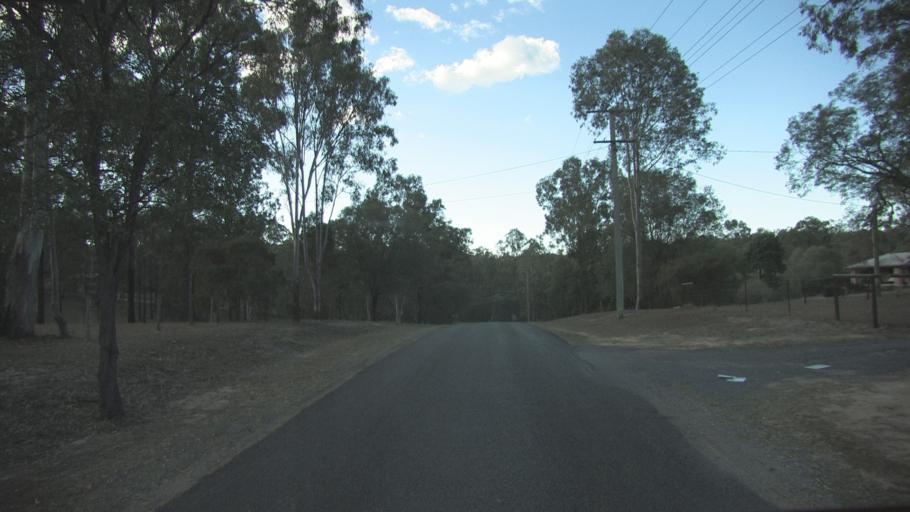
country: AU
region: Queensland
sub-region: Logan
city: Cedar Vale
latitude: -27.8478
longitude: 153.0909
